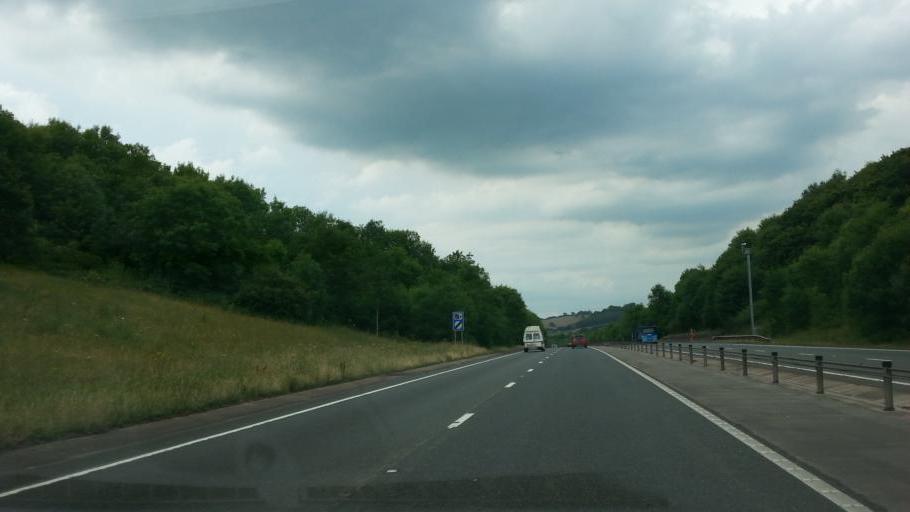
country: GB
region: Wales
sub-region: Monmouthshire
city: Llangybi
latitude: 51.6647
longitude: -2.8804
